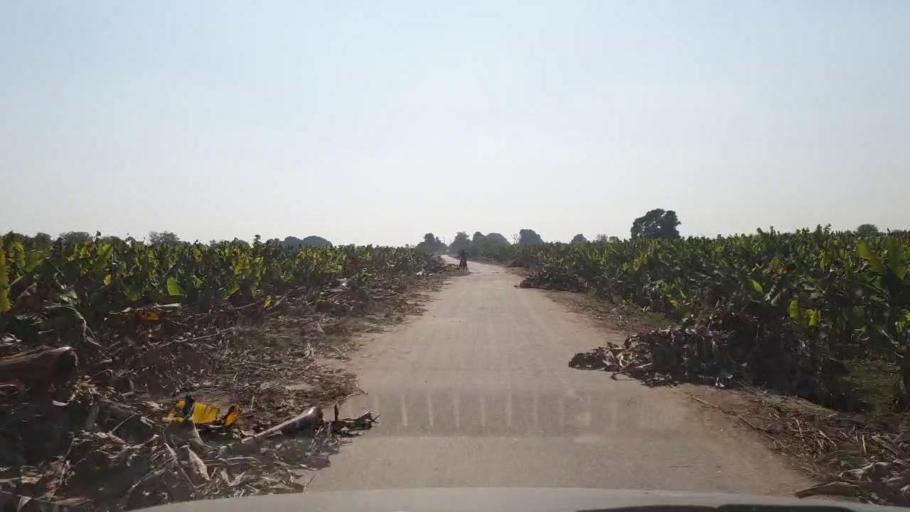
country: PK
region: Sindh
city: Tando Jam
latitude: 25.4173
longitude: 68.6316
